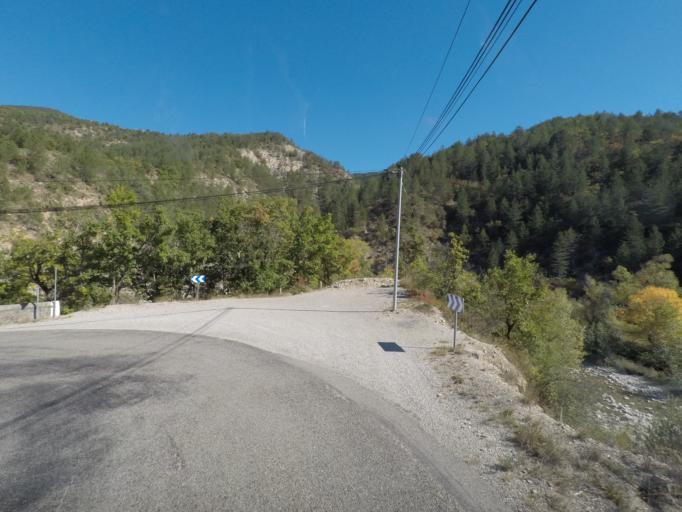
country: FR
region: Rhone-Alpes
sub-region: Departement de la Drome
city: Die
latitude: 44.6278
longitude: 5.3036
